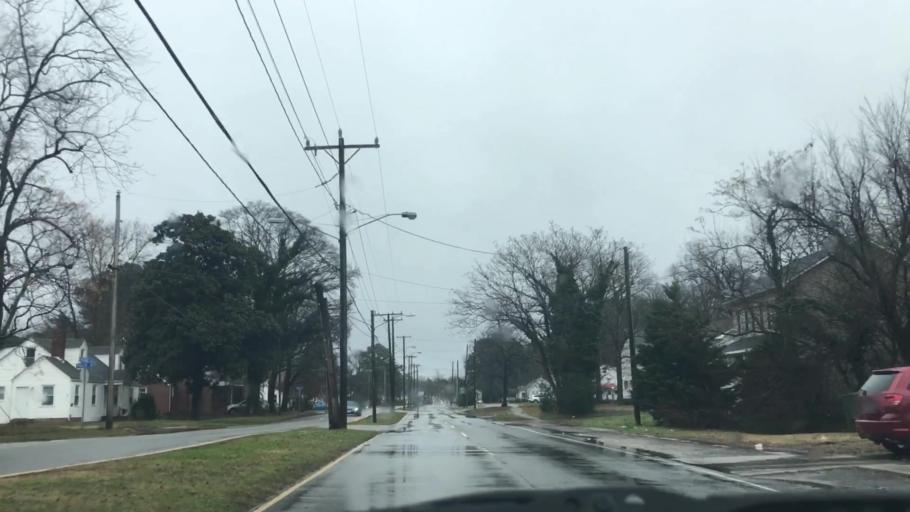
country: US
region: Virginia
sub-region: City of Norfolk
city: Norfolk
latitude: 36.8867
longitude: -76.2432
